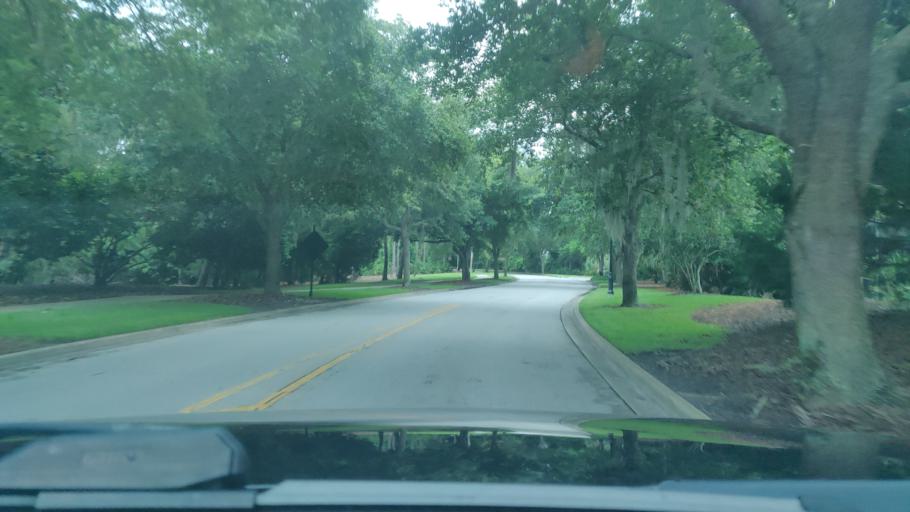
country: US
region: Florida
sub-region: Flagler County
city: Palm Coast
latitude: 29.5363
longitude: -81.1680
